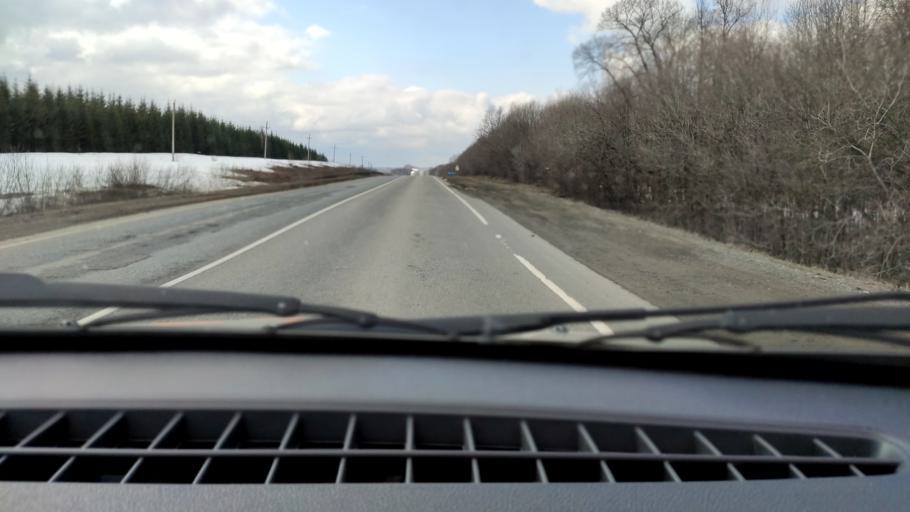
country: RU
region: Bashkortostan
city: Kudeyevskiy
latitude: 54.8047
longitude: 56.6225
